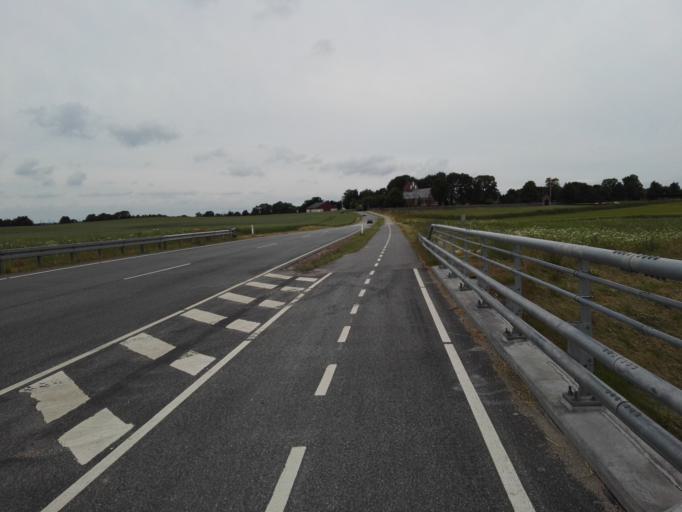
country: DK
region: Capital Region
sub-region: Egedal Kommune
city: Smorumnedre
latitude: 55.7320
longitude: 12.2826
